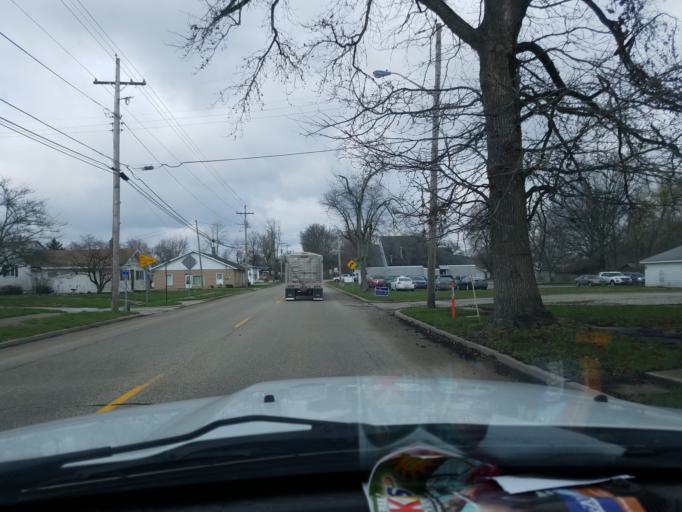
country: US
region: Indiana
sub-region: Vigo County
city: Seelyville
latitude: 39.3903
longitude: -87.3006
